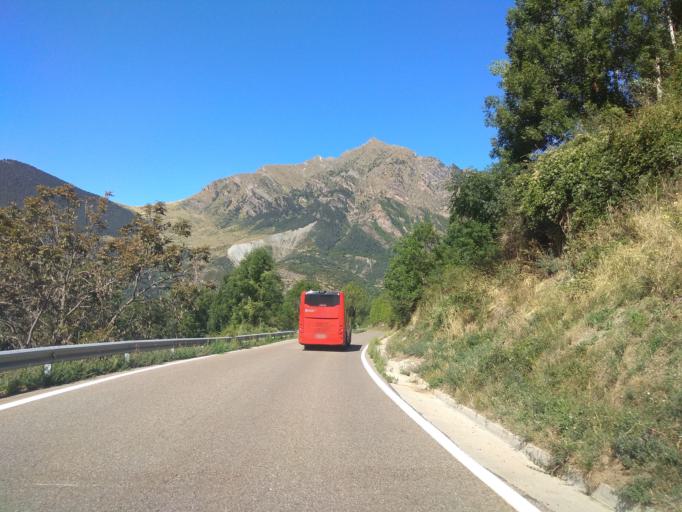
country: ES
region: Catalonia
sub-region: Provincia de Lleida
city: Vielha
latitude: 42.5204
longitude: 0.8448
